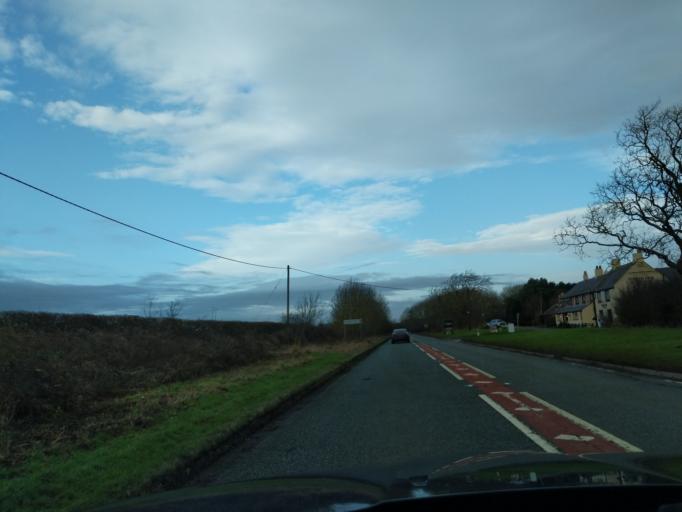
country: GB
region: England
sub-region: Northumberland
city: Darras Hall
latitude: 55.0756
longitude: -1.7983
